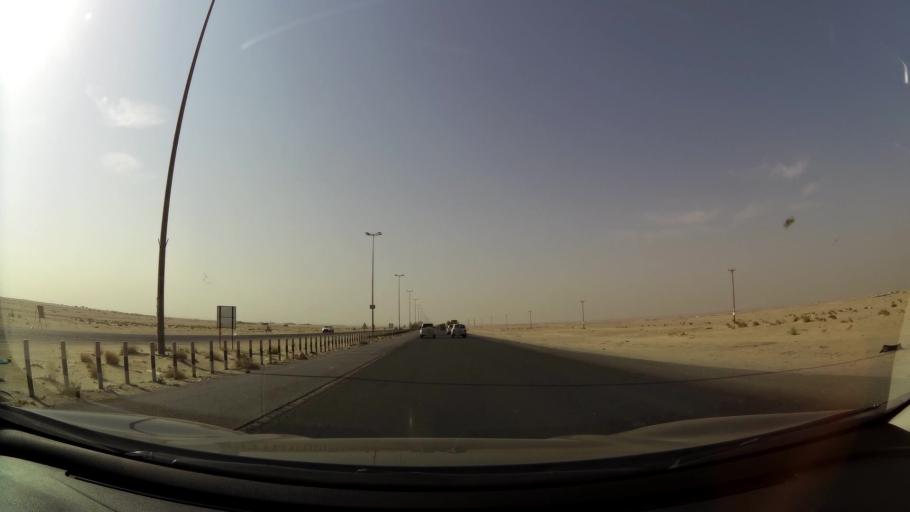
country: KW
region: Al Ahmadi
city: Al Ahmadi
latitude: 28.8810
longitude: 48.0804
